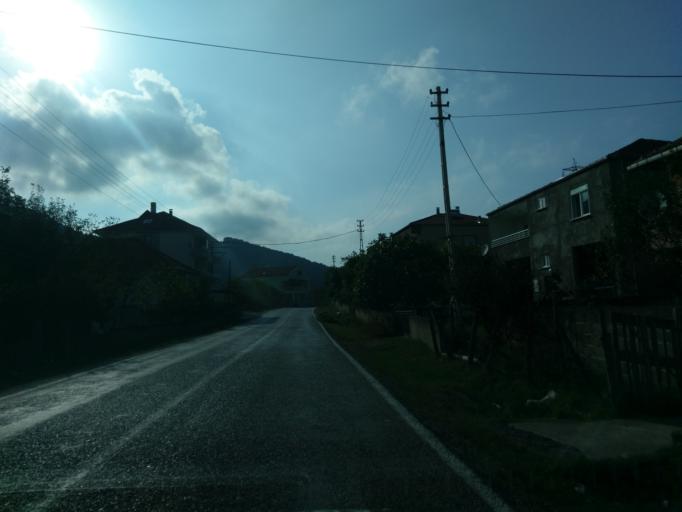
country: TR
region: Sinop
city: Helaldi
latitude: 41.9366
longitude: 34.4071
